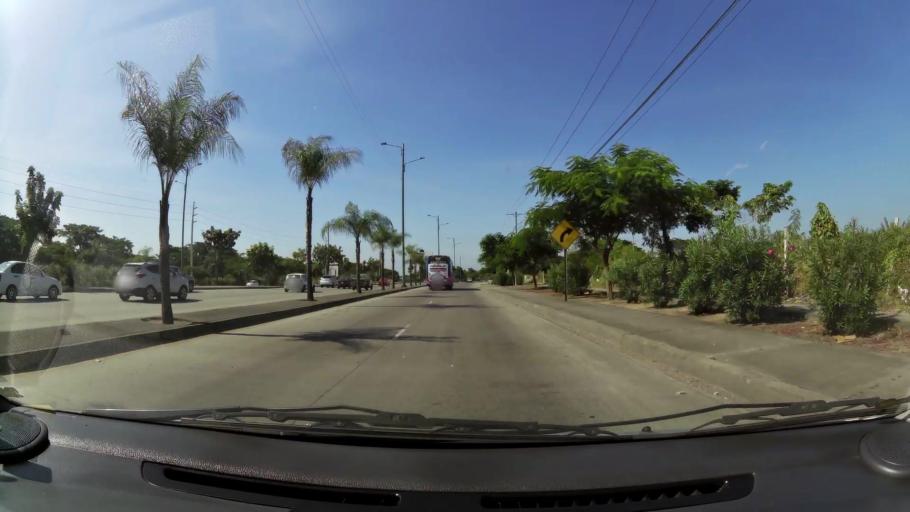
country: EC
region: Guayas
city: Eloy Alfaro
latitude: -2.1147
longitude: -79.8842
